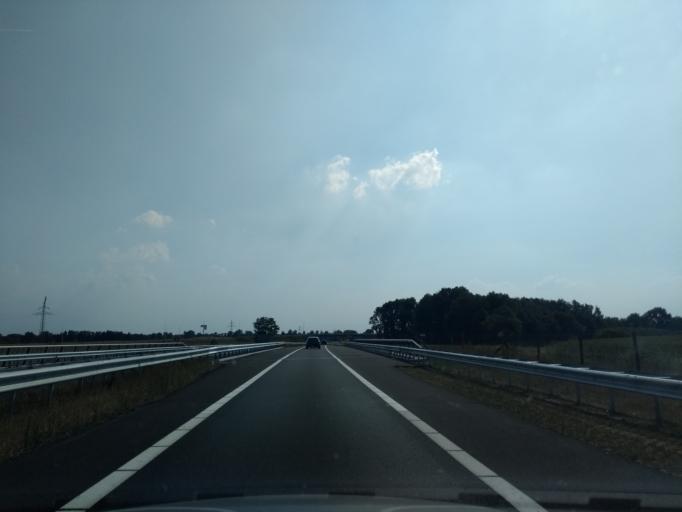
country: NL
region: Gelderland
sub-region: Berkelland
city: Eibergen
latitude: 52.1376
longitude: 6.6759
